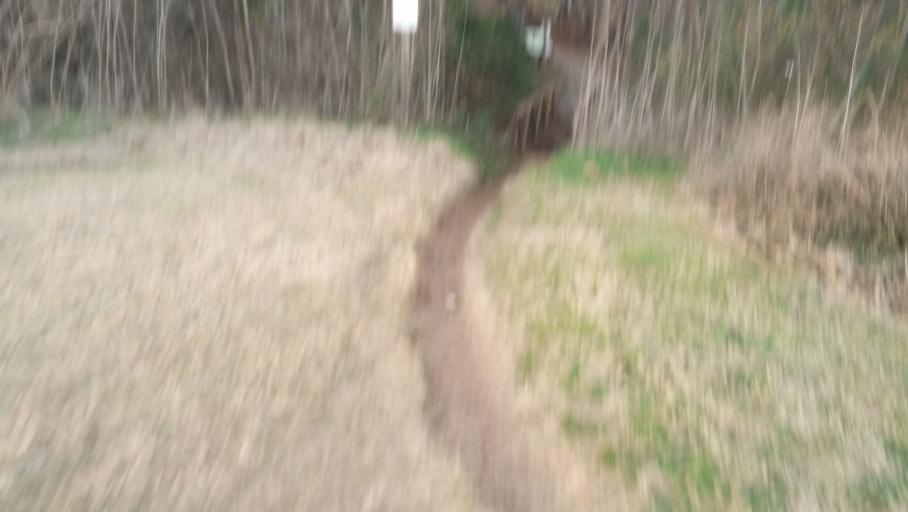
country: US
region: Texas
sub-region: Nacogdoches County
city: Nacogdoches
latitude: 31.6276
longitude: -94.6427
